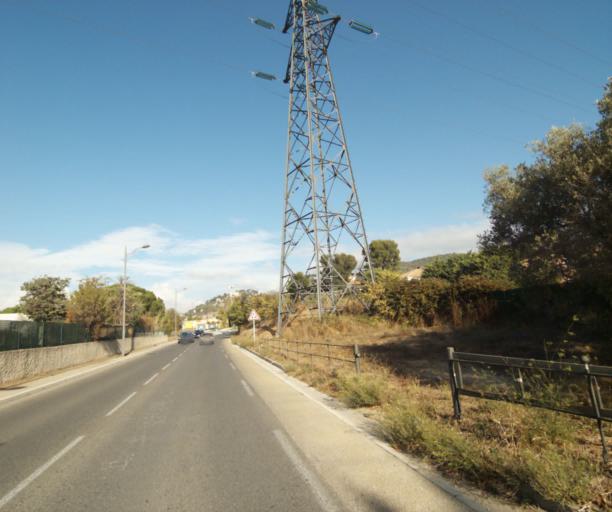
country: FR
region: Provence-Alpes-Cote d'Azur
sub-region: Departement des Bouches-du-Rhone
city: Allauch
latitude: 43.3268
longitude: 5.4910
